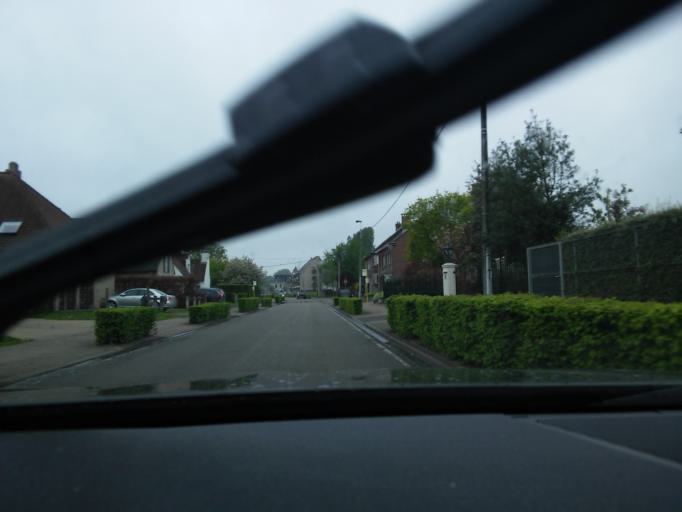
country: BE
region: Flanders
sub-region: Provincie Vlaams-Brabant
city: Sint-Pieters-Leeuw
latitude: 50.8095
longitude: 4.2361
